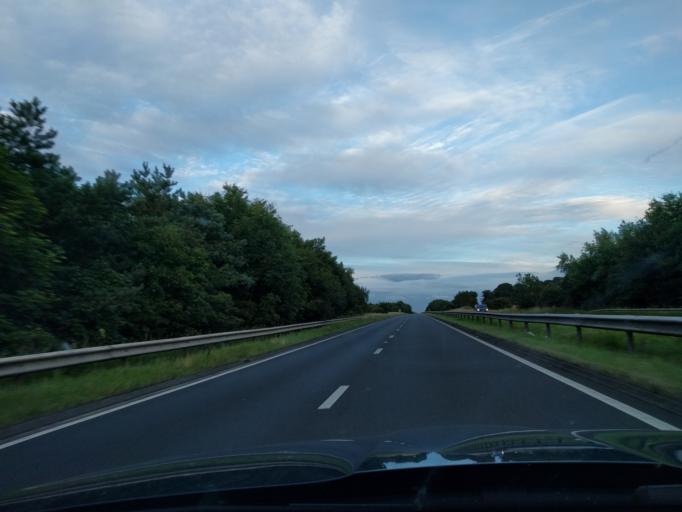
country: GB
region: England
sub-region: Northumberland
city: Morpeth
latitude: 55.1448
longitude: -1.6967
